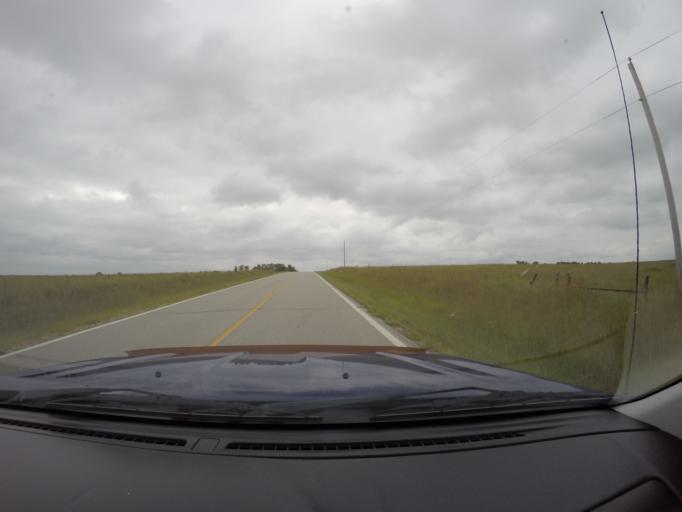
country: US
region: Kansas
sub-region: Morris County
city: Council Grove
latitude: 38.8407
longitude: -96.5072
